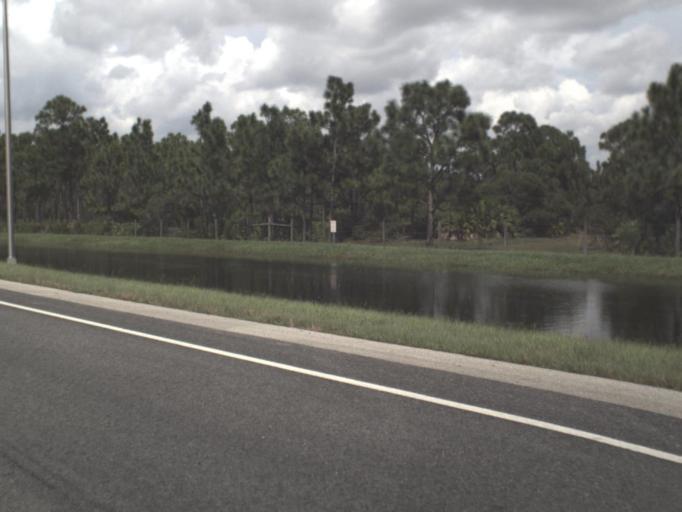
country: US
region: Florida
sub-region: Charlotte County
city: Charlotte Park
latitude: 26.8852
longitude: -81.9914
